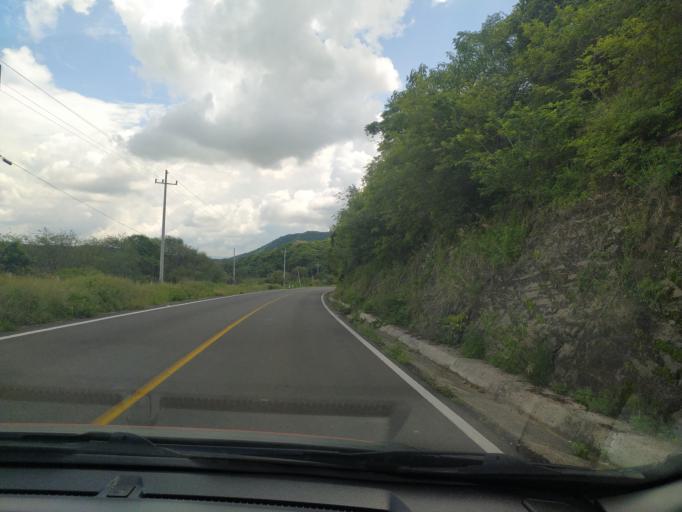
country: MX
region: Jalisco
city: Villa Corona
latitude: 20.3902
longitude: -103.6739
